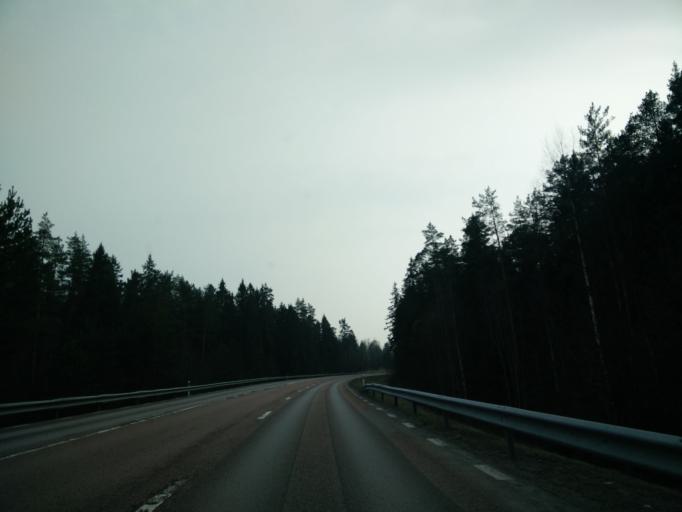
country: SE
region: Vaermland
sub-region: Forshaga Kommun
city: Forshaga
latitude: 59.5464
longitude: 13.4697
